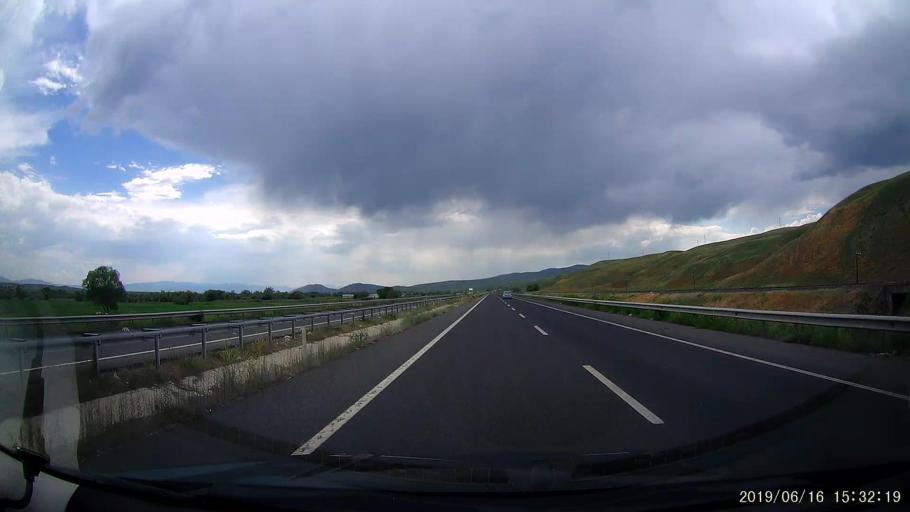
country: TR
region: Erzurum
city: Horasan
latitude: 40.0300
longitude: 42.0514
